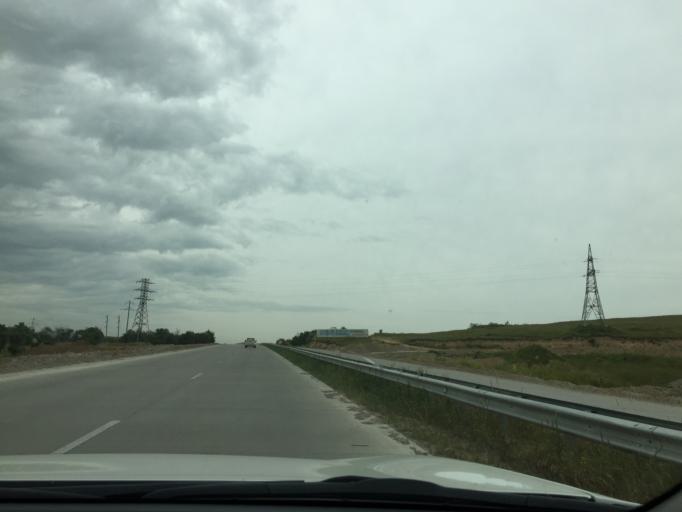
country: KZ
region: Ongtustik Qazaqstan
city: Sastobe
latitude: 42.5324
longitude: 70.0214
